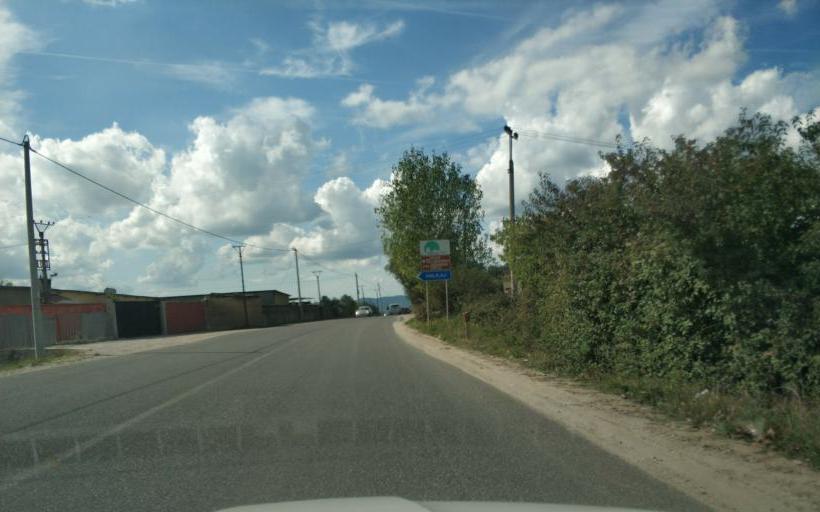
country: AL
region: Durres
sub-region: Rrethi i Krujes
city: Nikel
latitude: 41.4806
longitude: 19.7630
